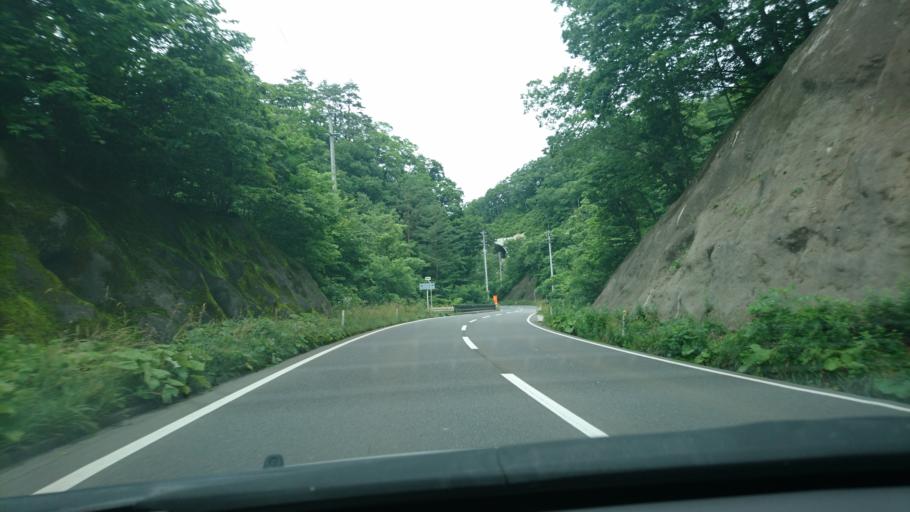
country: JP
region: Iwate
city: Miyako
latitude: 39.9841
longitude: 141.8639
